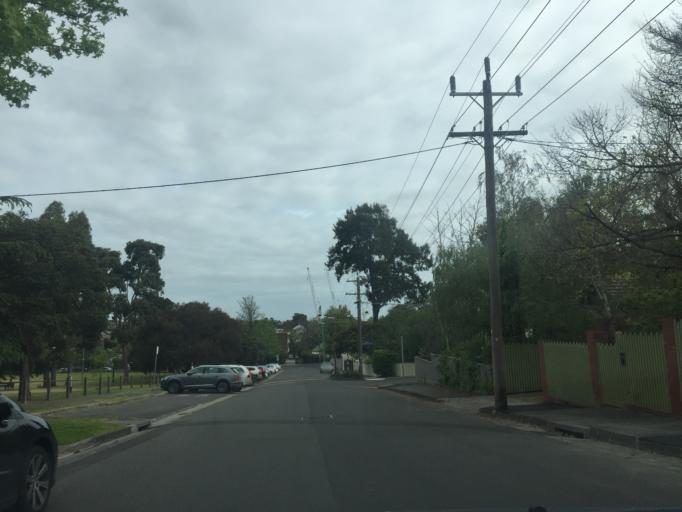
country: AU
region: Victoria
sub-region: Boroondara
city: Hawthorn East
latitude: -37.8191
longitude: 145.0522
